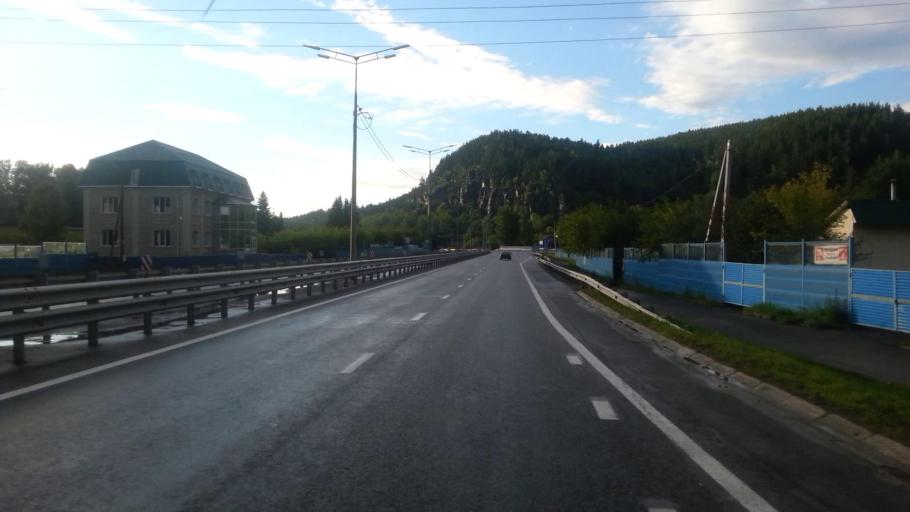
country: RU
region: Altay
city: Souzga
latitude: 51.9159
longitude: 85.8614
